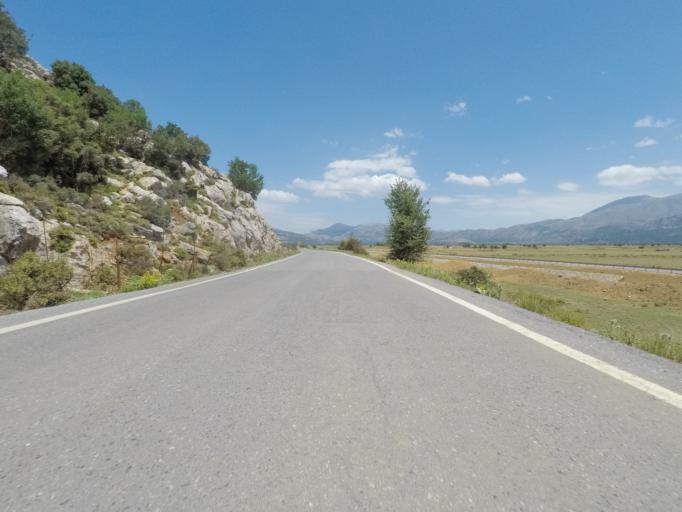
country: GR
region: Crete
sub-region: Nomos Irakleiou
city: Mokhos
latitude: 35.1933
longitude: 25.4351
